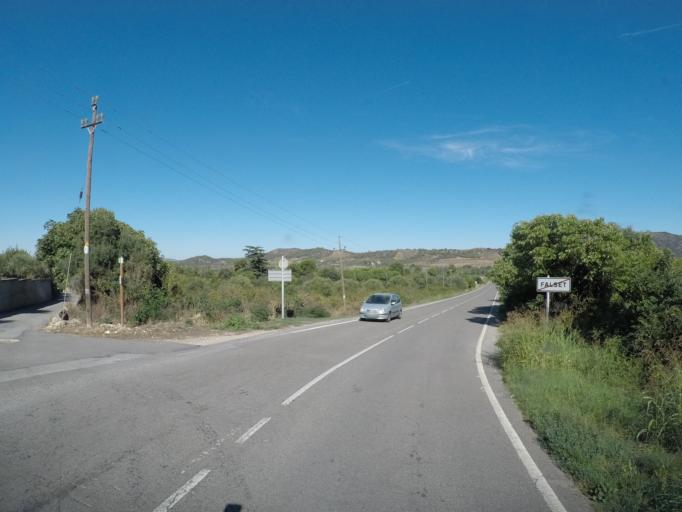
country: ES
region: Catalonia
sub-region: Provincia de Tarragona
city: Falset
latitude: 41.1473
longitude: 0.8195
